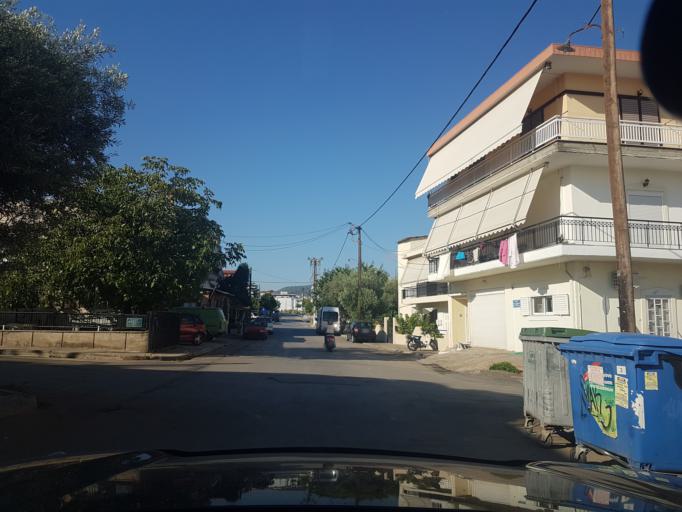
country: GR
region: Central Greece
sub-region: Nomos Evvoias
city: Chalkida
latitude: 38.4729
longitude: 23.5849
